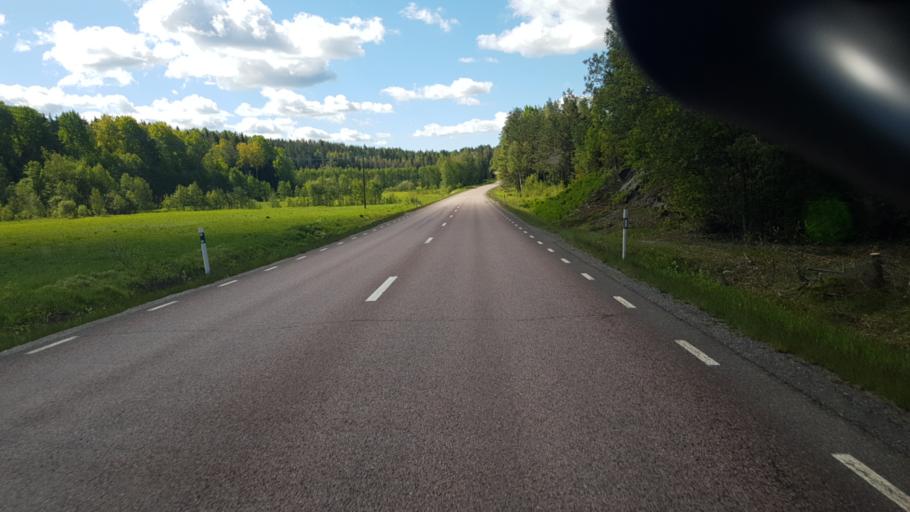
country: SE
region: Vaermland
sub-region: Arvika Kommun
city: Arvika
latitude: 59.6115
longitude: 12.6190
